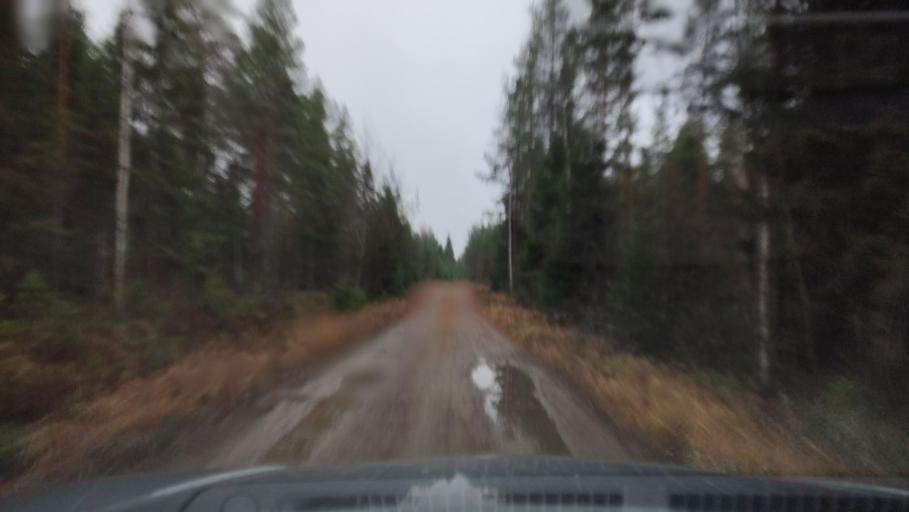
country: FI
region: Southern Ostrobothnia
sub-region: Suupohja
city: Karijoki
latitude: 62.1594
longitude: 21.5898
